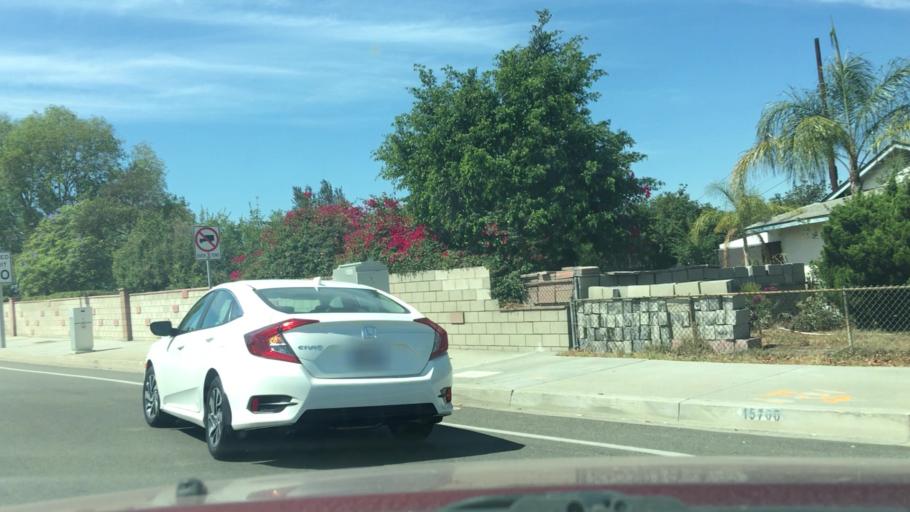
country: US
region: California
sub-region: Orange County
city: Buena Park
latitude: 33.8883
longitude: -117.9994
